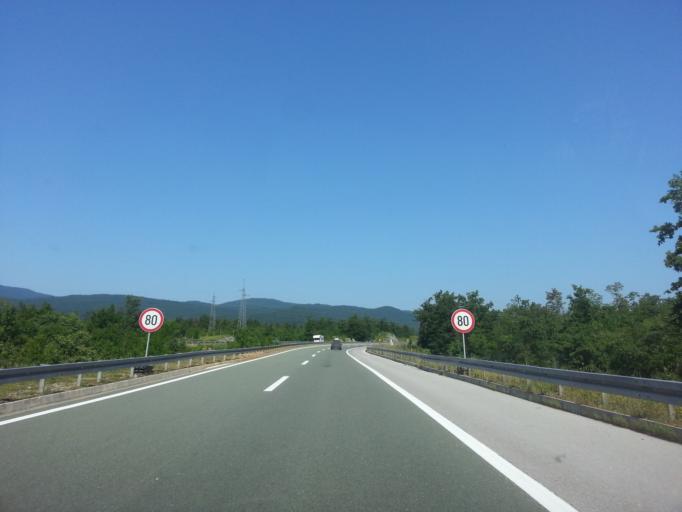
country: HR
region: Primorsko-Goranska
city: Matulji
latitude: 45.4274
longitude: 14.2955
